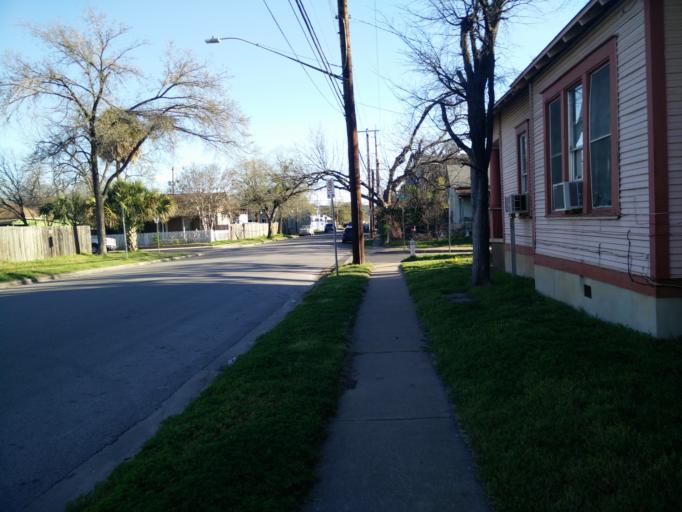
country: US
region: Texas
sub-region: Travis County
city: Austin
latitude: 30.2574
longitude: -97.7291
